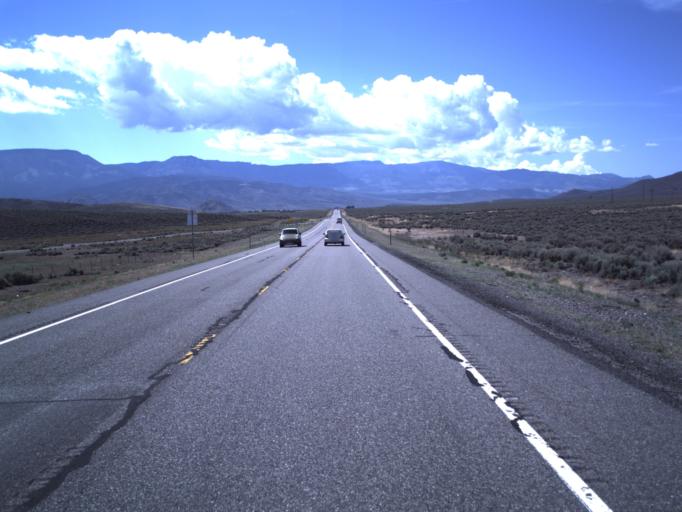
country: US
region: Utah
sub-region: Piute County
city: Junction
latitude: 38.2794
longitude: -112.2241
